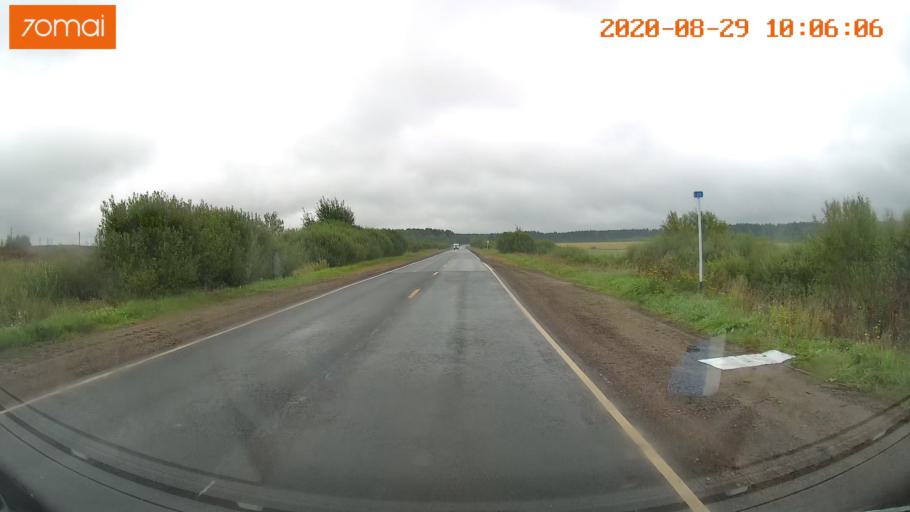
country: RU
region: Ivanovo
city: Zarechnyy
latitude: 57.3897
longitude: 42.5399
